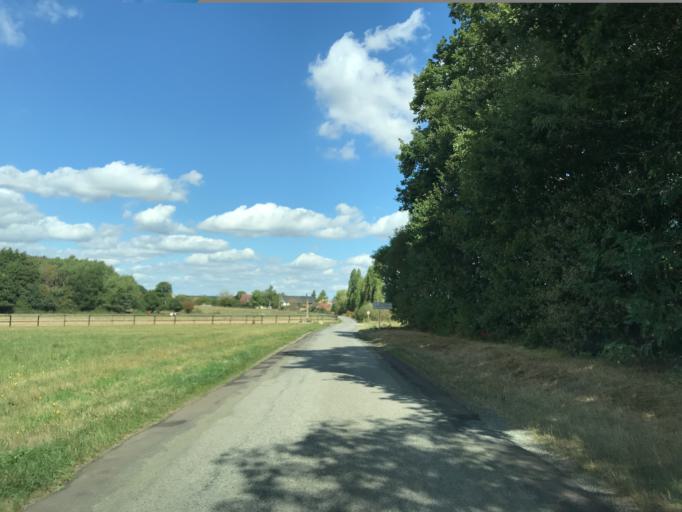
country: FR
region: Haute-Normandie
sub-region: Departement de l'Eure
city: La Chapelle-Reanville
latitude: 49.1010
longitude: 1.3901
